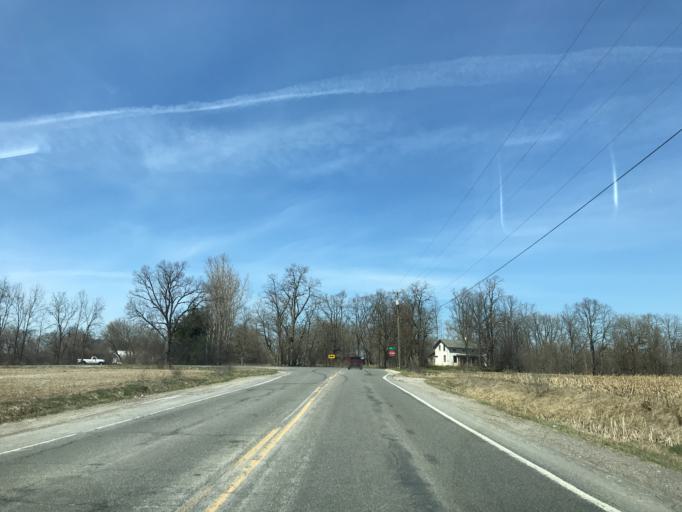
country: US
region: Michigan
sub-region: Washtenaw County
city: Ann Arbor
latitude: 42.3419
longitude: -83.7086
